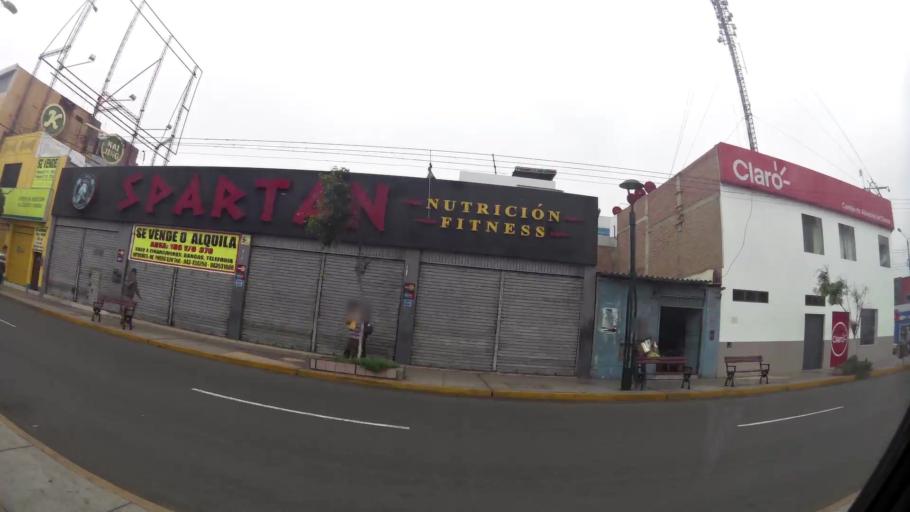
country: PE
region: Ancash
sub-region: Provincia de Santa
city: Chimbote
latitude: -9.0773
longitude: -78.5909
